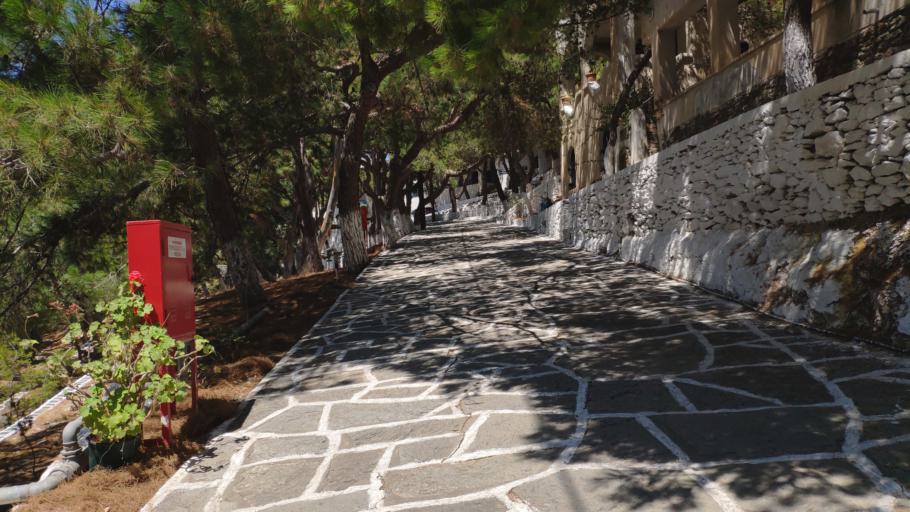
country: GR
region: South Aegean
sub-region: Nomos Kykladon
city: Kythnos
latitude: 37.3453
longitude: 24.4364
